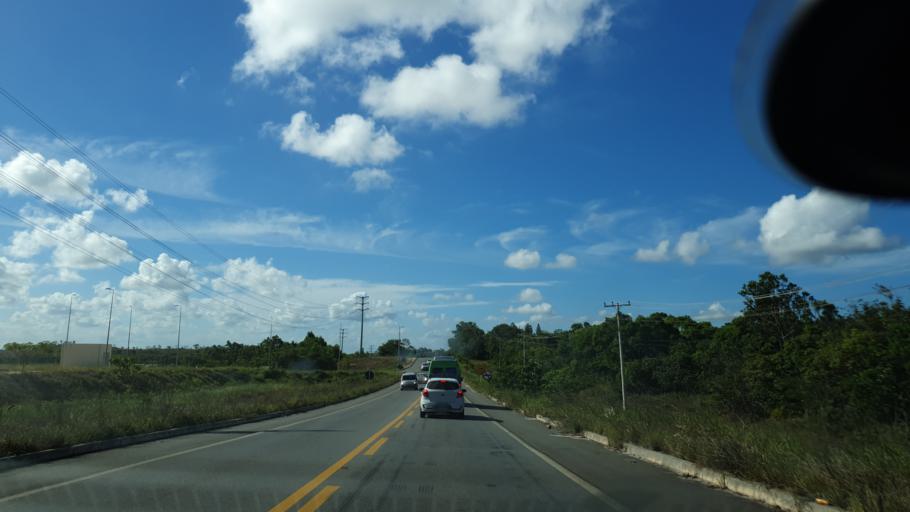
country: BR
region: Bahia
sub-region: Camacari
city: Camacari
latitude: -12.6927
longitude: -38.2242
